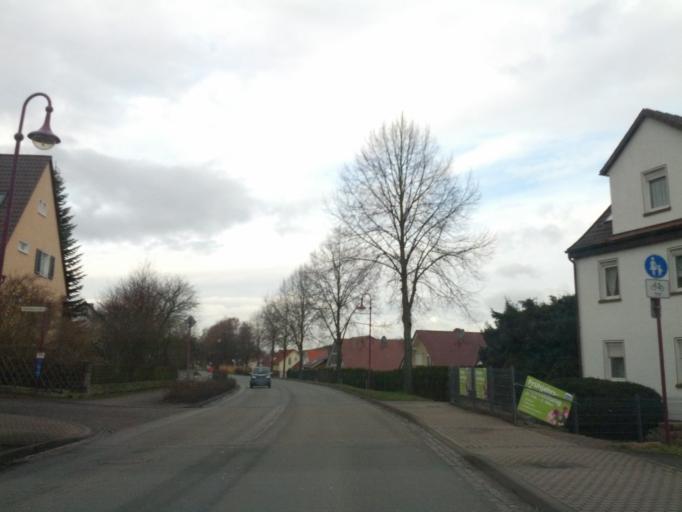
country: DE
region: Hesse
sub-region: Regierungsbezirk Kassel
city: Kaufungen
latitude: 51.2846
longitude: 9.6258
